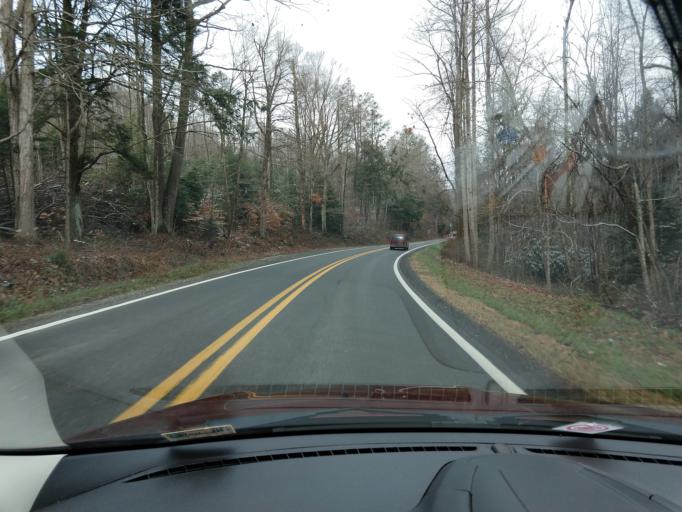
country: US
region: West Virginia
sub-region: Nicholas County
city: Craigsville
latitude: 38.2567
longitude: -80.7279
